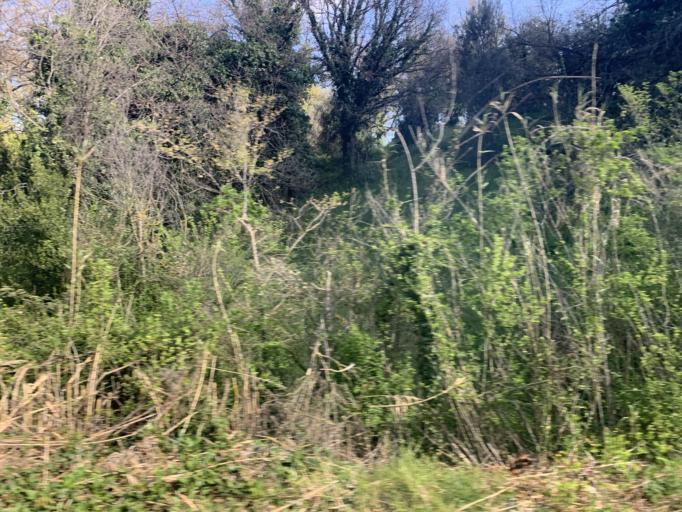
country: IT
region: Latium
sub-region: Citta metropolitana di Roma Capitale
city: Marino
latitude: 41.7780
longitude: 12.6373
